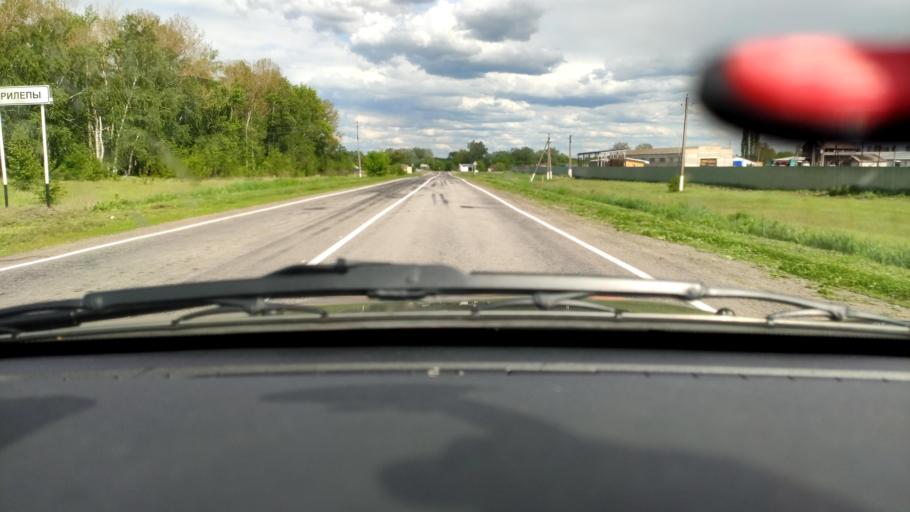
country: RU
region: Voronezj
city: Ostrogozhsk
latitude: 51.0557
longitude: 38.9061
